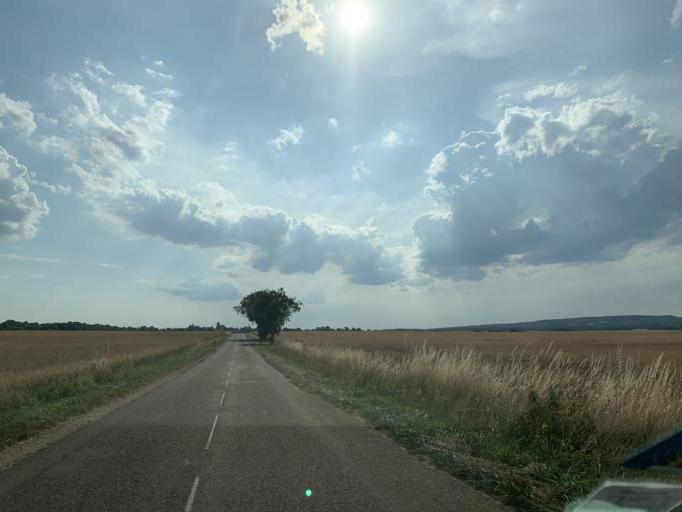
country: FR
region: Bourgogne
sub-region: Departement de l'Yonne
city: Fontenailles
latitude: 47.5081
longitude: 3.3691
